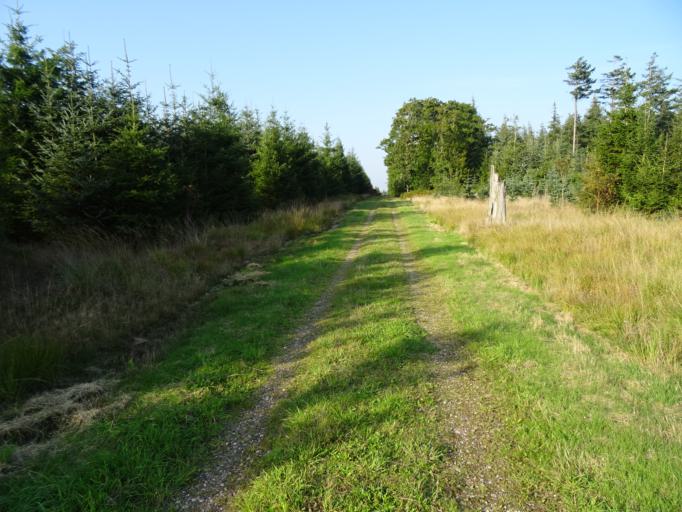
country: DK
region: South Denmark
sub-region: Tonder Kommune
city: Toftlund
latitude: 55.1960
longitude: 8.9452
